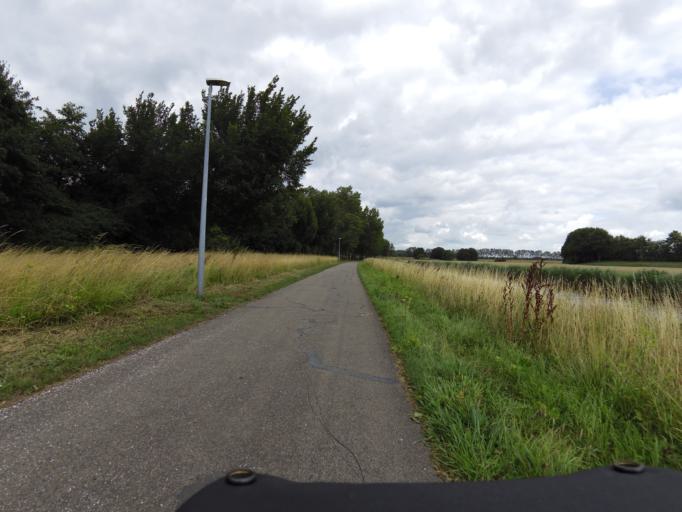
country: NL
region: South Holland
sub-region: Gemeente Goeree-Overflakkee
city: Goedereede
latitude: 51.8263
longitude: 4.0015
